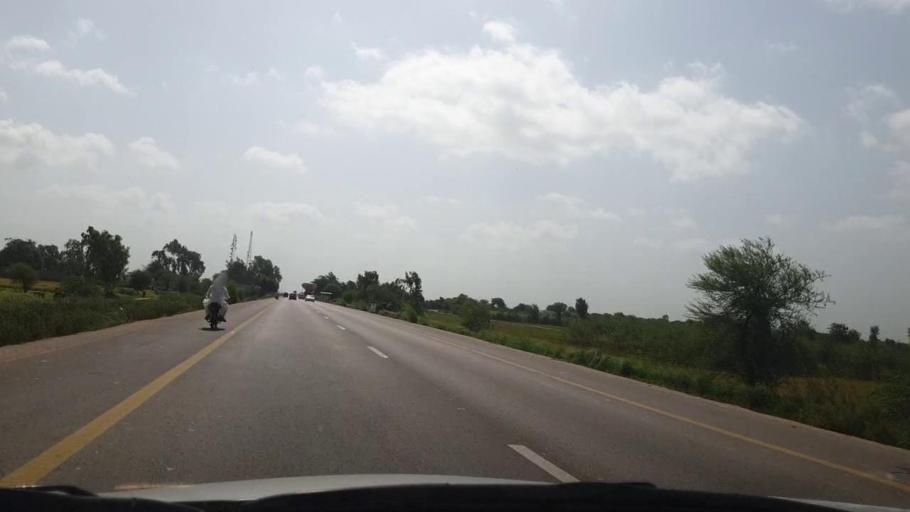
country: PK
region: Sindh
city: Matli
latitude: 24.9443
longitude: 68.7003
